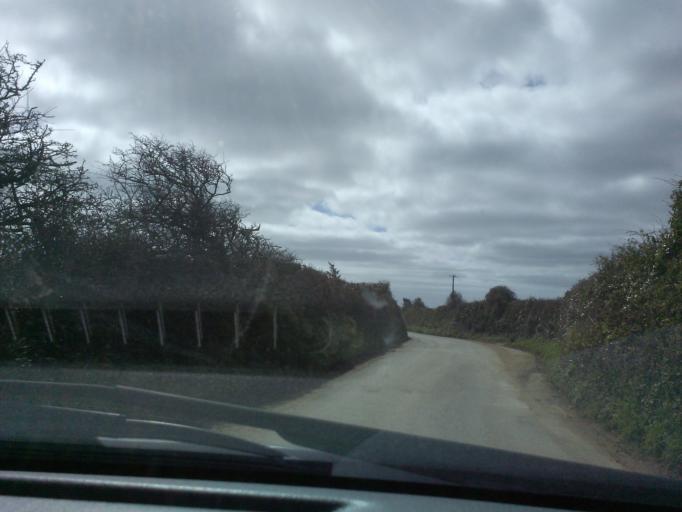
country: GB
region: England
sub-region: Cornwall
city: St. Buryan
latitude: 50.0615
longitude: -5.6047
